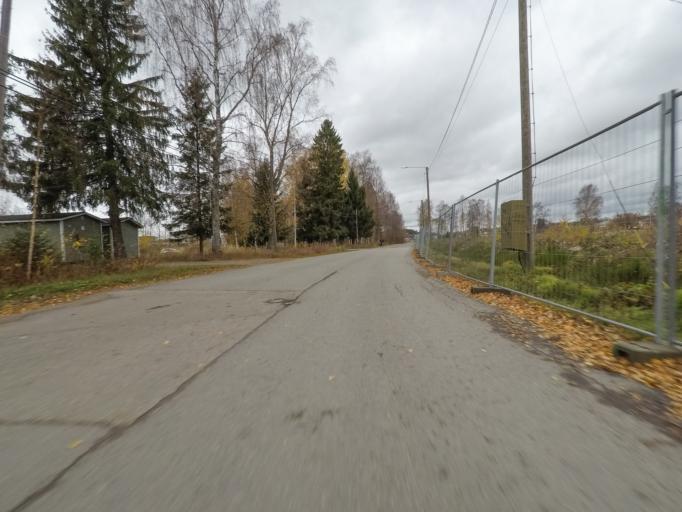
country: FI
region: Uusimaa
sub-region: Porvoo
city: Porvoo
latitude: 60.3844
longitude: 25.6624
